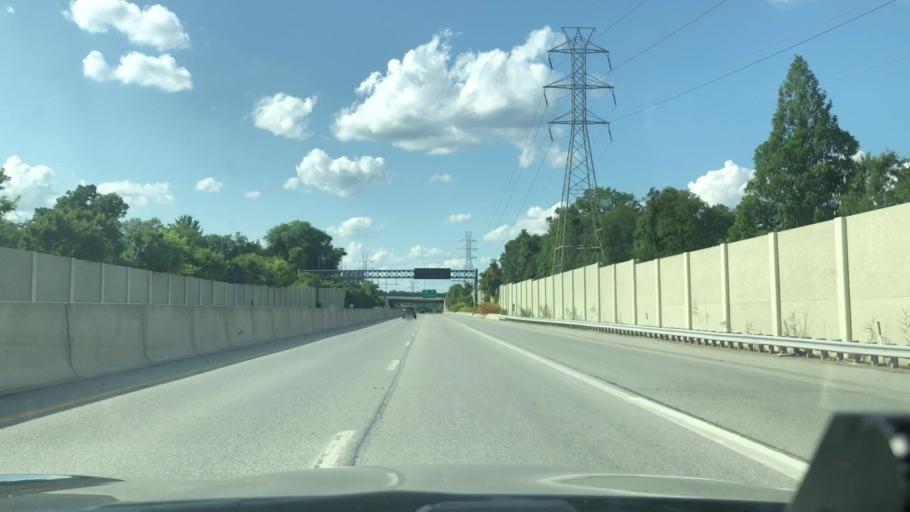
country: US
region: Pennsylvania
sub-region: Montgomery County
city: Flourtown
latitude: 40.1166
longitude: -75.2025
